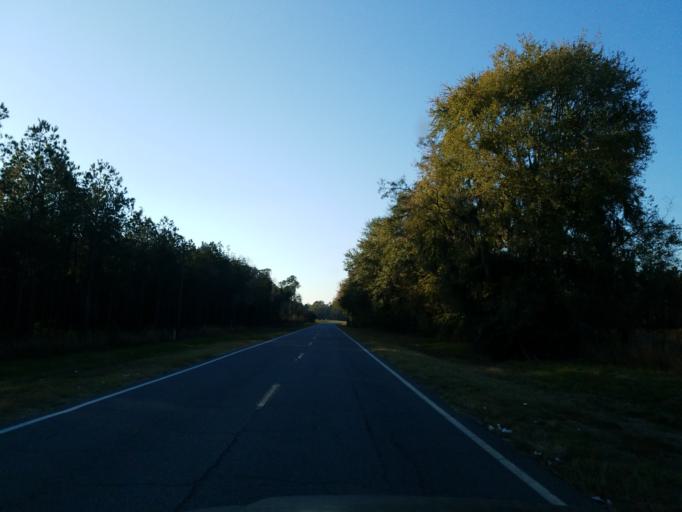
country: US
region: Georgia
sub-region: Berrien County
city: Nashville
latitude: 31.1905
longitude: -83.2049
